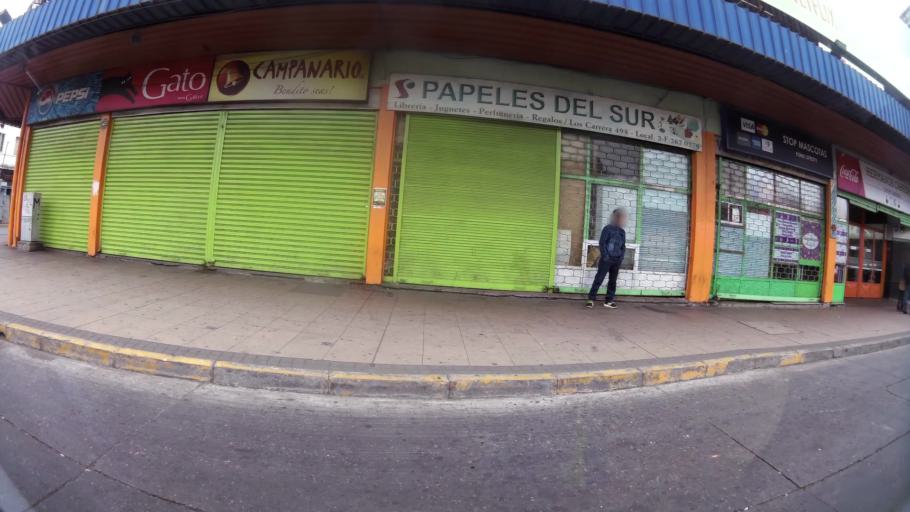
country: CL
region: Biobio
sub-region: Provincia de Concepcion
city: Concepcion
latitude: -36.8245
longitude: -73.0545
